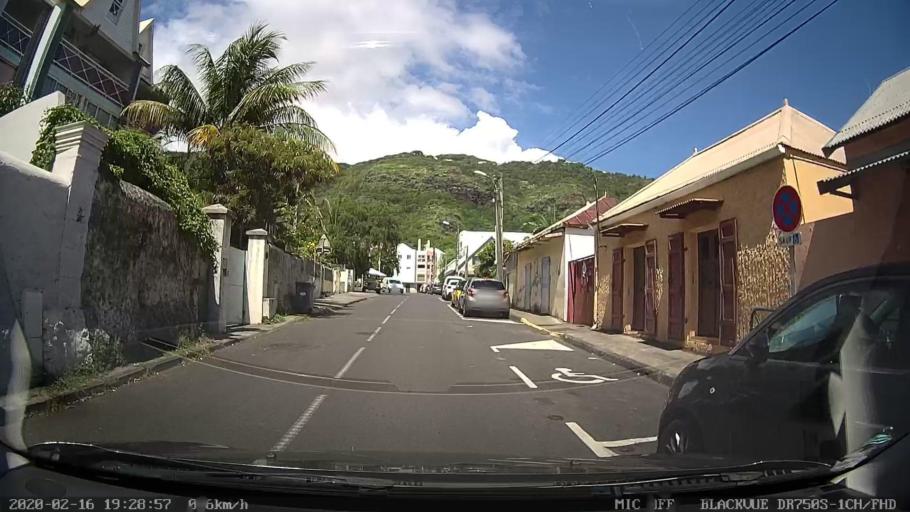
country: RE
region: Reunion
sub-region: Reunion
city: Saint-Denis
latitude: -20.8805
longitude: 55.4433
